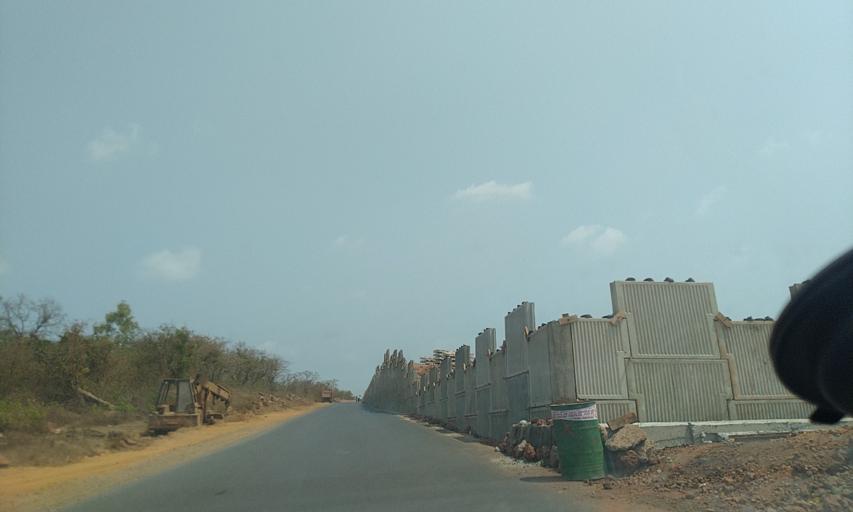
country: IN
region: Goa
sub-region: North Goa
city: Colovale
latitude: 15.6824
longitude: 73.8342
